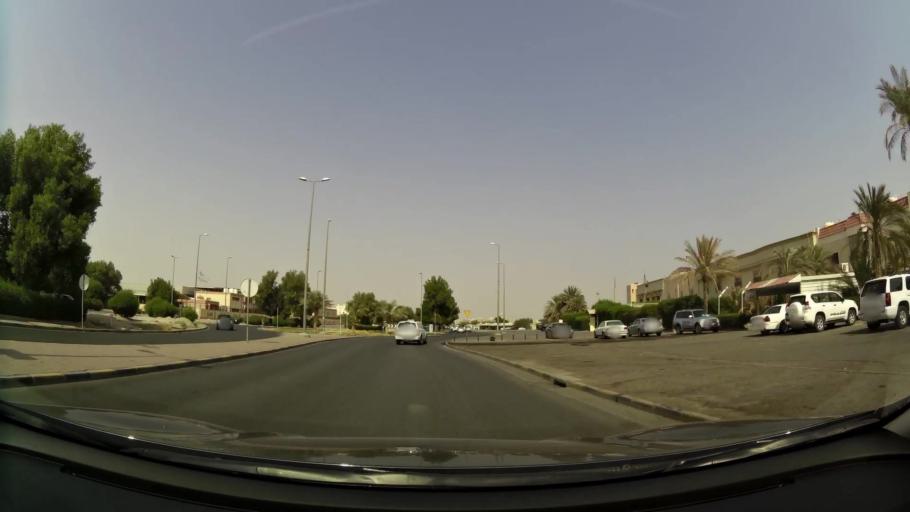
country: KW
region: Muhafazat al Jahra'
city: Al Jahra'
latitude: 29.3272
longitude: 47.6626
